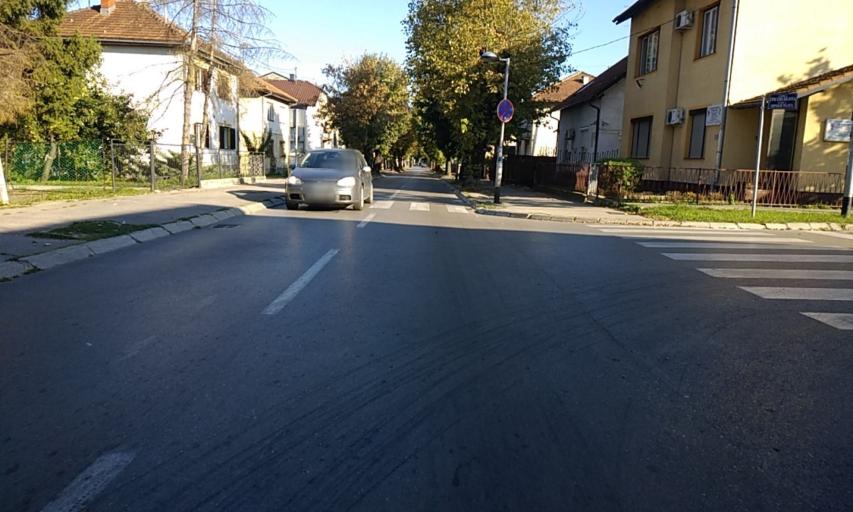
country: BA
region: Republika Srpska
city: Banja Luka
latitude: 44.7827
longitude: 17.1945
